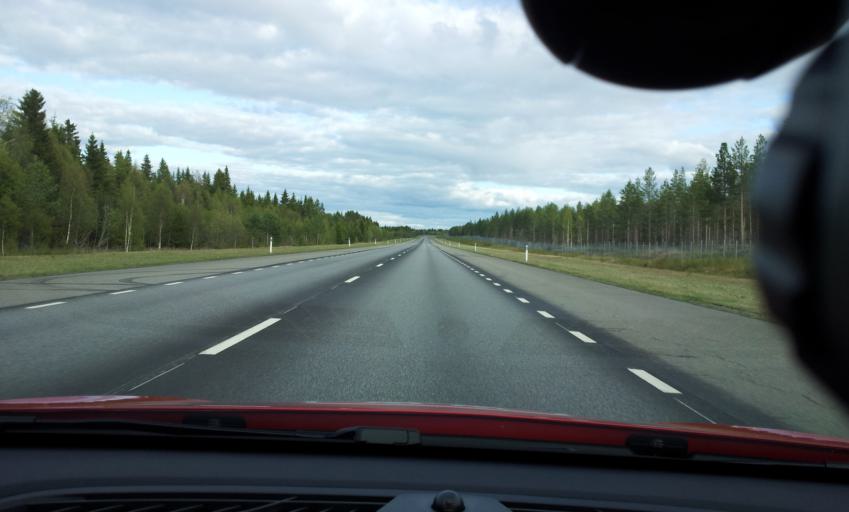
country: SE
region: Jaemtland
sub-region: OEstersunds Kommun
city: Ostersund
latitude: 63.1986
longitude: 14.5069
